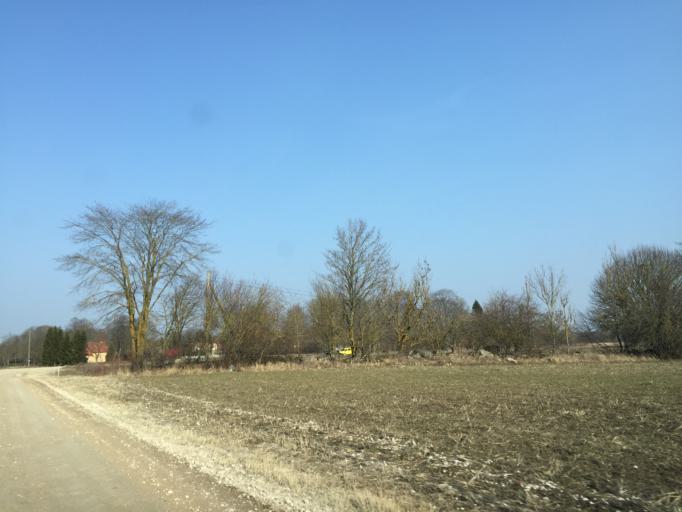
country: EE
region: Saare
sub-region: Kuressaare linn
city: Kuressaare
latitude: 58.3785
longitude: 22.6893
